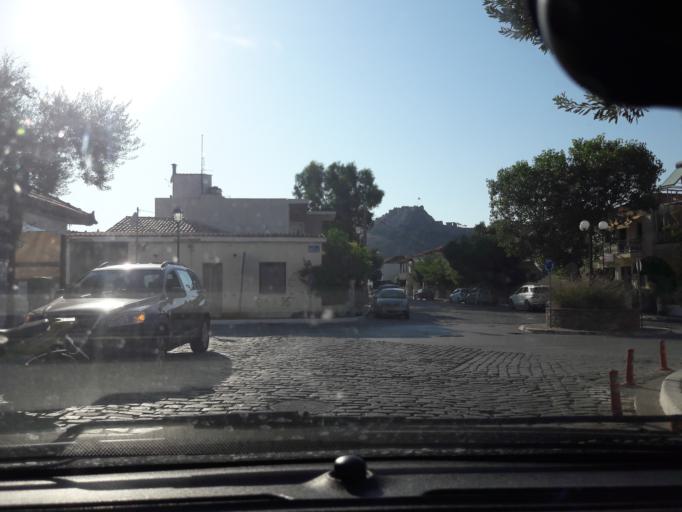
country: GR
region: North Aegean
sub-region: Nomos Lesvou
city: Myrina
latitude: 39.8730
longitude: 25.0623
